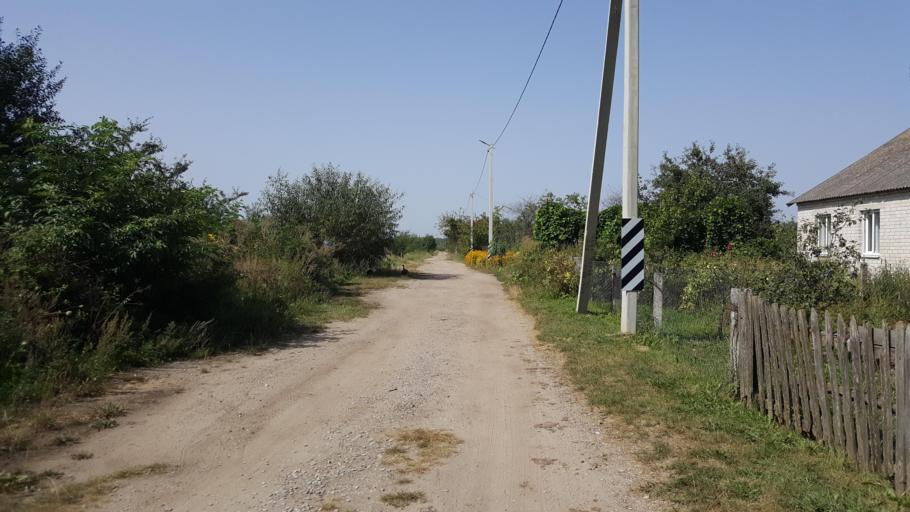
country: BY
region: Brest
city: Pruzhany
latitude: 52.4921
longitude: 24.6098
